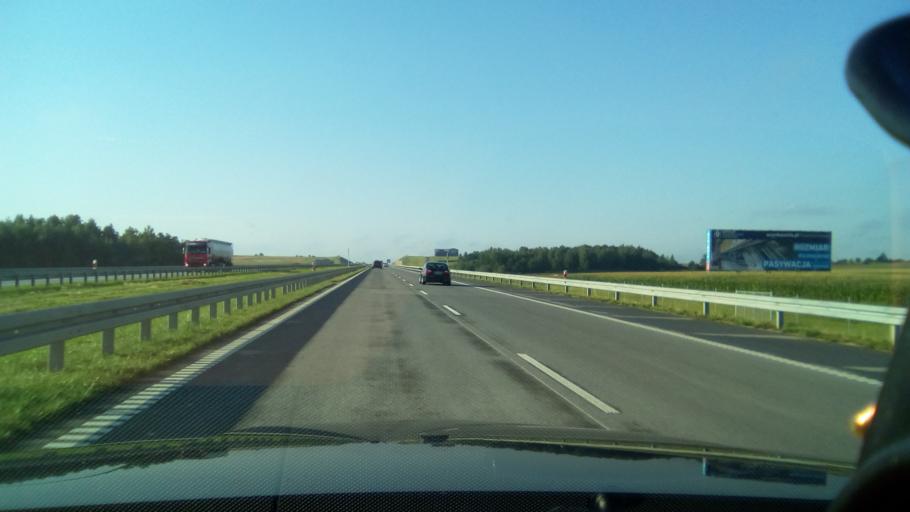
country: PL
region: Silesian Voivodeship
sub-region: Powiat czestochowski
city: Starcza
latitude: 50.6296
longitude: 19.0336
